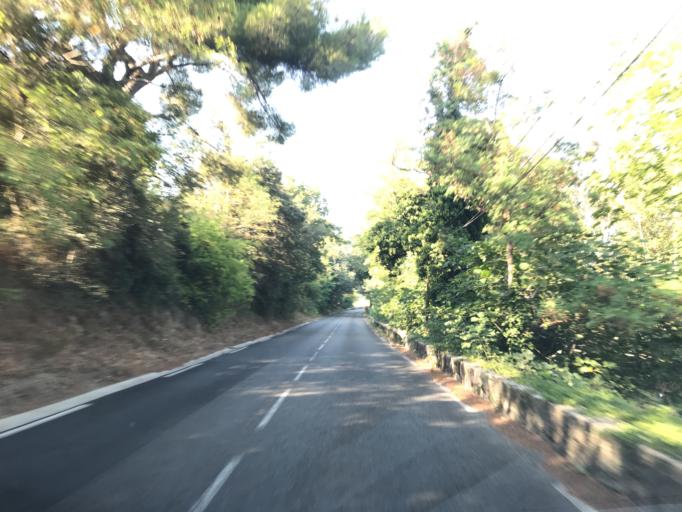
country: FR
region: Provence-Alpes-Cote d'Azur
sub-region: Departement des Bouches-du-Rhone
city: Saint-Chamas
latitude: 43.5543
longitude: 5.0124
